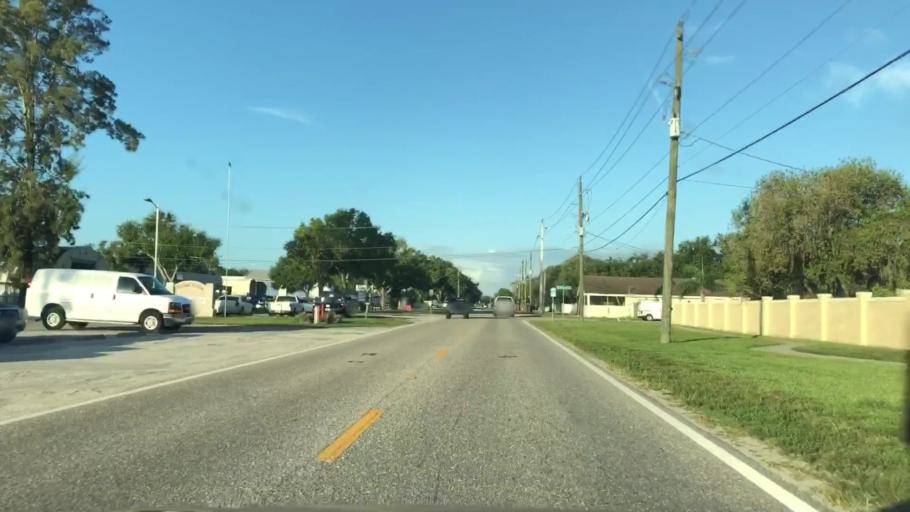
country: US
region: Florida
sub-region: Sarasota County
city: Fruitville
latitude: 27.3269
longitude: -82.4567
